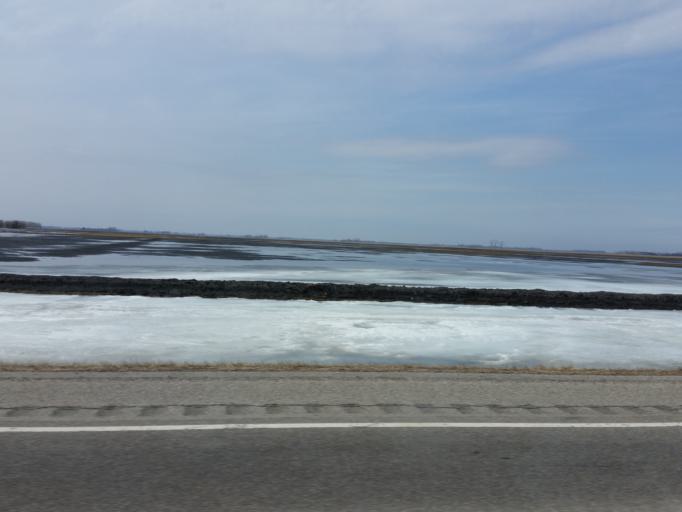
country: US
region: North Dakota
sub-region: Walsh County
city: Grafton
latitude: 48.3483
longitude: -97.4051
